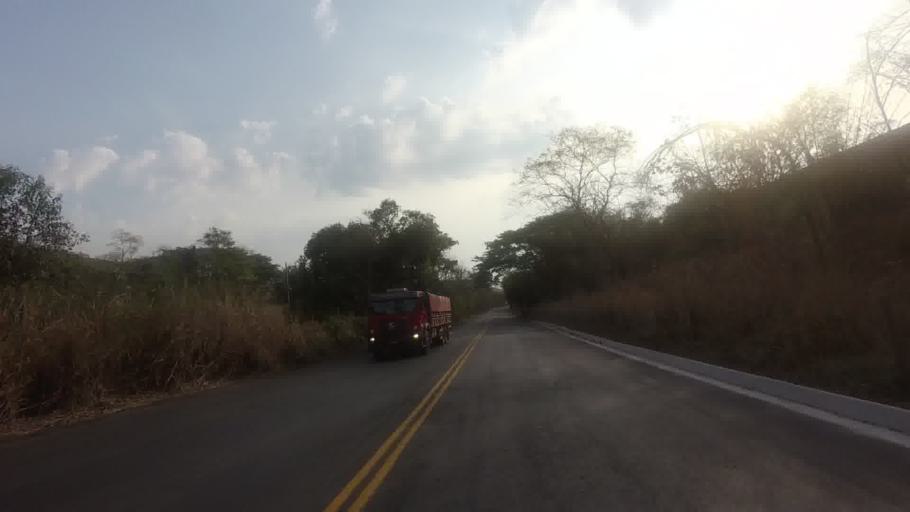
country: BR
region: Rio de Janeiro
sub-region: Cambuci
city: Cambuci
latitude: -21.4557
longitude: -42.0144
